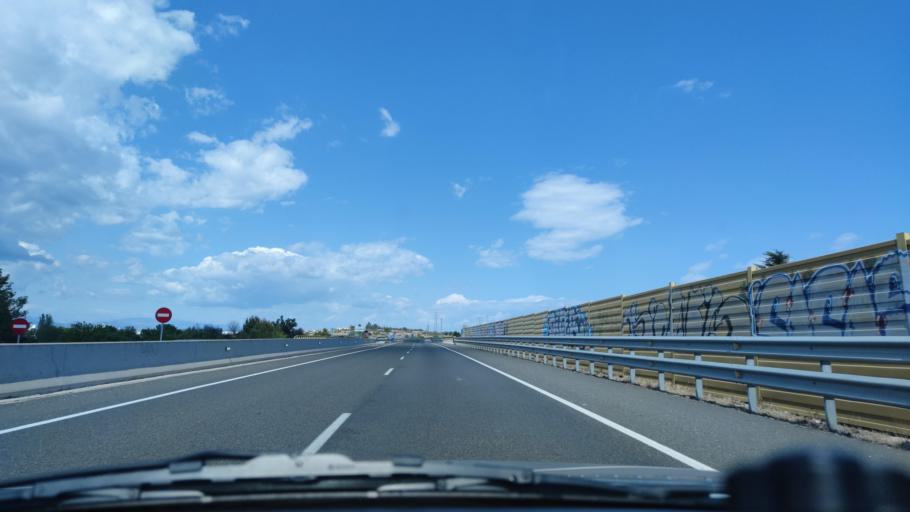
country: ES
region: Catalonia
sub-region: Provincia de Lleida
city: Lleida
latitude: 41.5933
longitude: 0.6441
